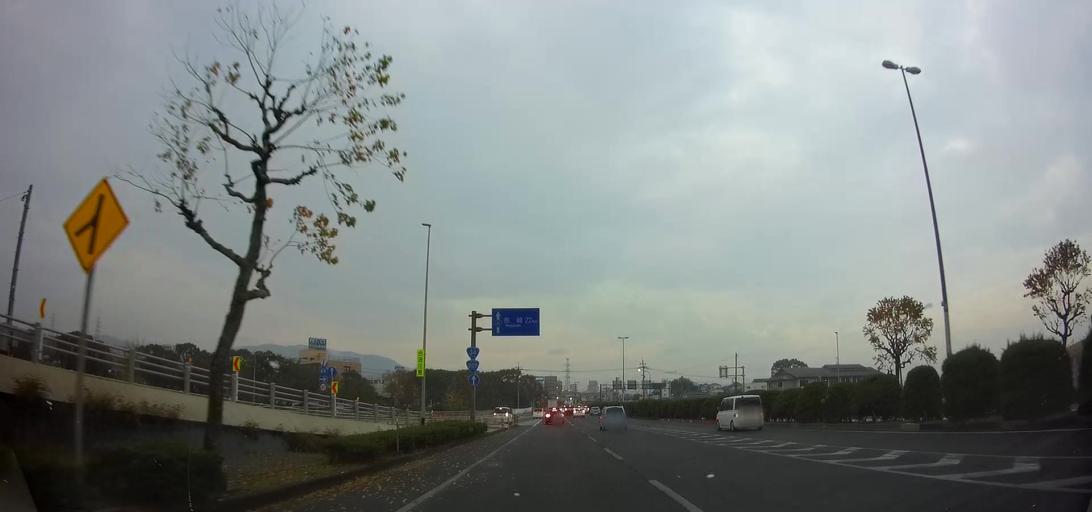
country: JP
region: Nagasaki
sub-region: Isahaya-shi
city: Isahaya
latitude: 32.8386
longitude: 130.0222
